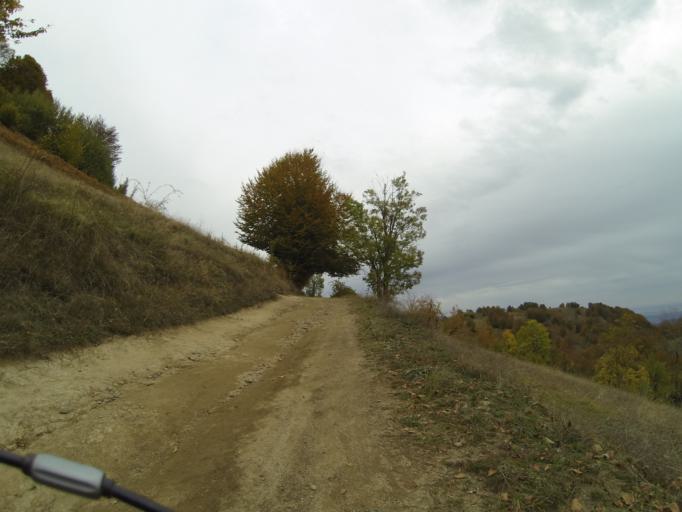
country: RO
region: Gorj
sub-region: Comuna Pades
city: Closani
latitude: 45.1024
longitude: 22.8420
